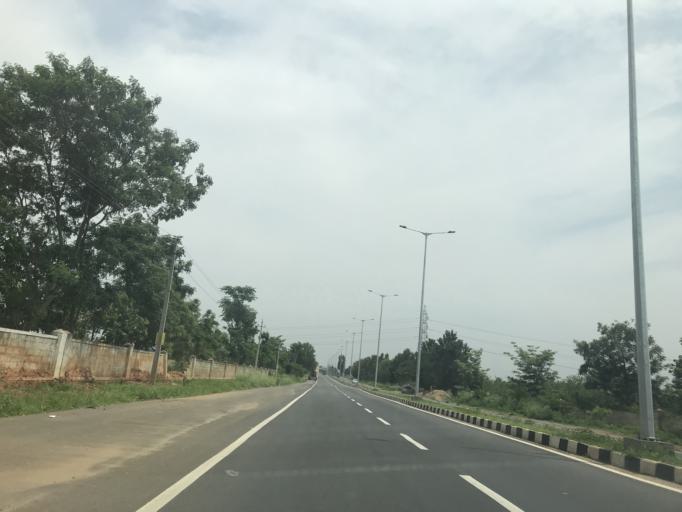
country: IN
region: Karnataka
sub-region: Bangalore Urban
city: Yelahanka
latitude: 13.1122
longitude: 77.6672
